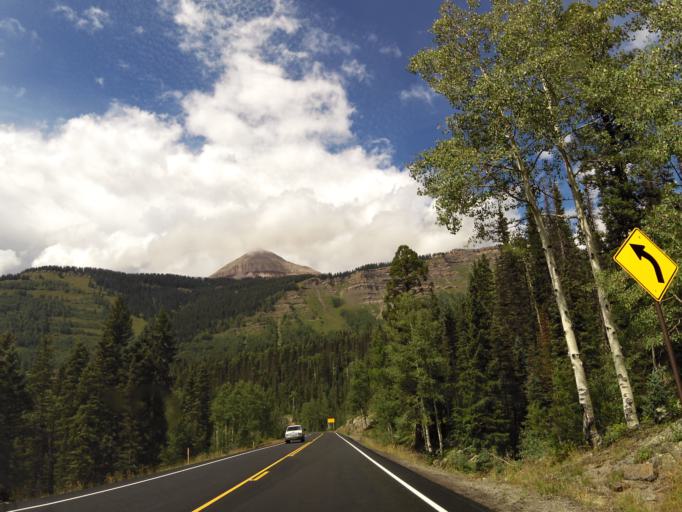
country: US
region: Colorado
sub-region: San Juan County
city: Silverton
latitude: 37.6786
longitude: -107.7842
